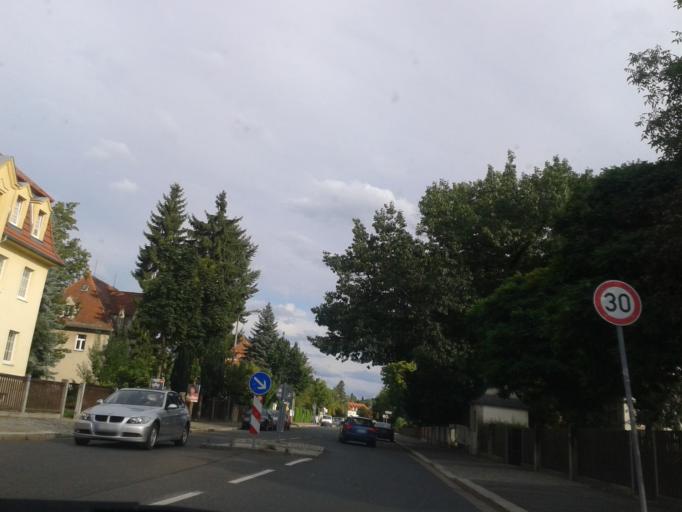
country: DE
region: Saxony
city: Dresden
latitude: 51.0182
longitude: 13.7596
